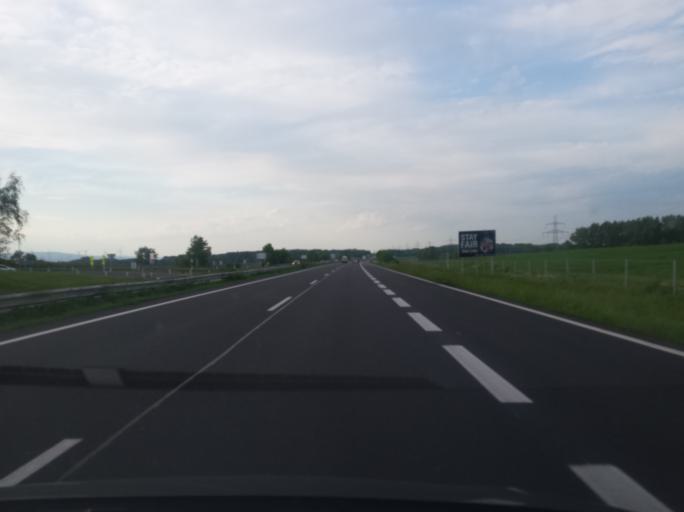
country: AT
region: Burgenland
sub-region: Eisenstadt-Umgebung
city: Hornstein
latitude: 47.8781
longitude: 16.4160
